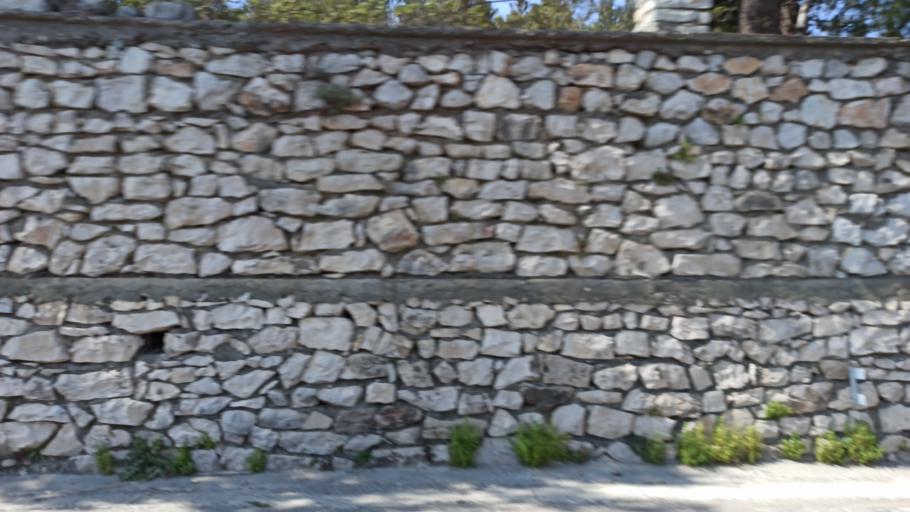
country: AL
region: Shkoder
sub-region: Rrethi i Malesia e Madhe
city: Kuc
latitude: 42.0569
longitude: 19.5436
